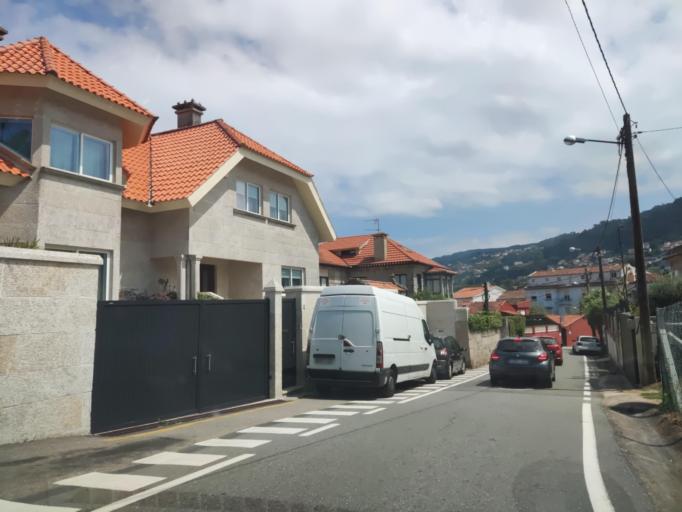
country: ES
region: Galicia
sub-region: Provincia de Pontevedra
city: Vigo
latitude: 42.2523
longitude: -8.6953
